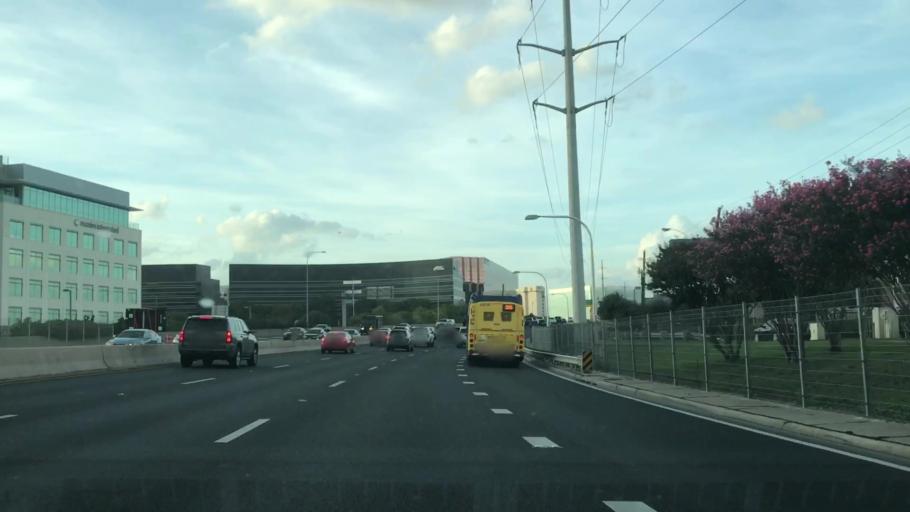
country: US
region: Texas
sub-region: Dallas County
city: Addison
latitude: 32.9454
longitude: -96.8230
